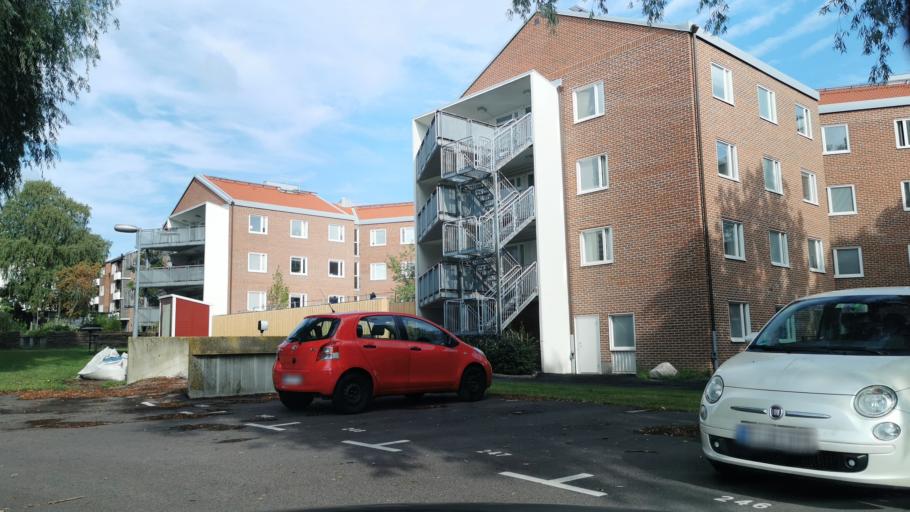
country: SE
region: Vaestra Goetaland
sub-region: Goteborg
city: Majorna
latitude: 57.6583
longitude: 11.9314
